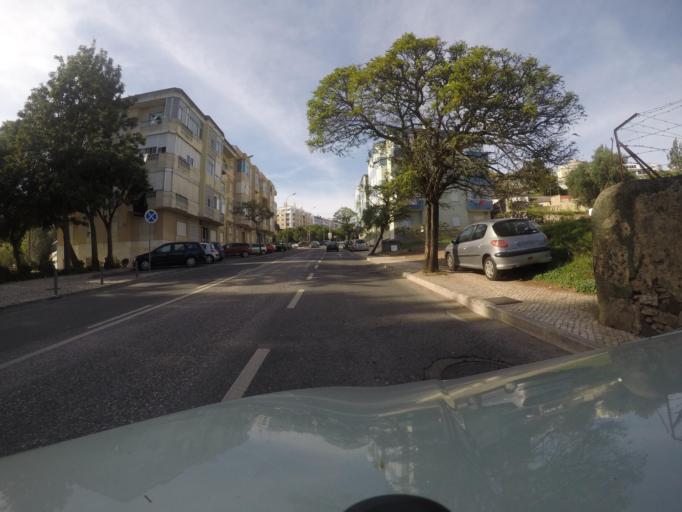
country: PT
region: Lisbon
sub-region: Amadora
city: Amadora
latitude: 38.7630
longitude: -9.2290
